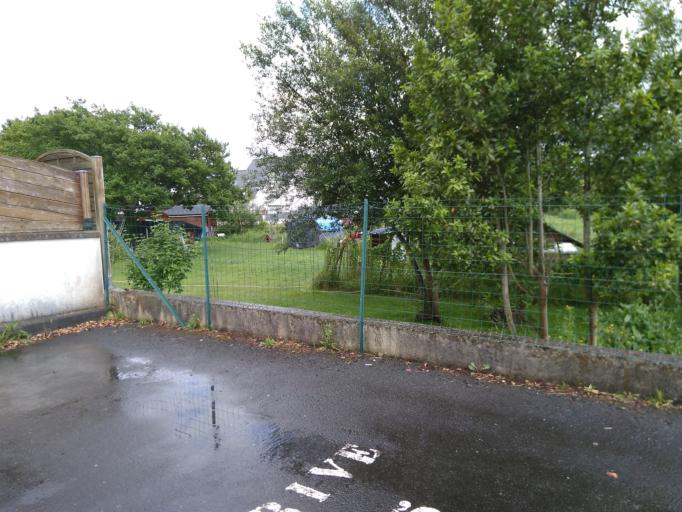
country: FR
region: Brittany
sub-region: Departement des Cotes-d'Armor
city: Lancieux
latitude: 48.6043
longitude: -2.1578
